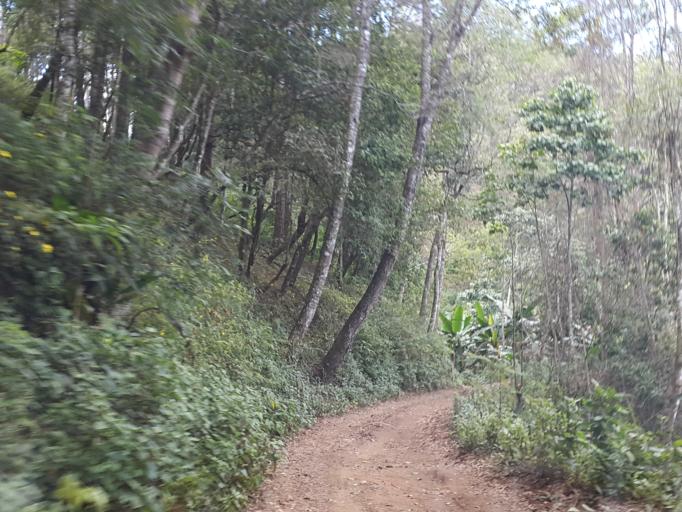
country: TH
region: Chiang Mai
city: Wiang Haeng
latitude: 19.5514
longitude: 98.8147
